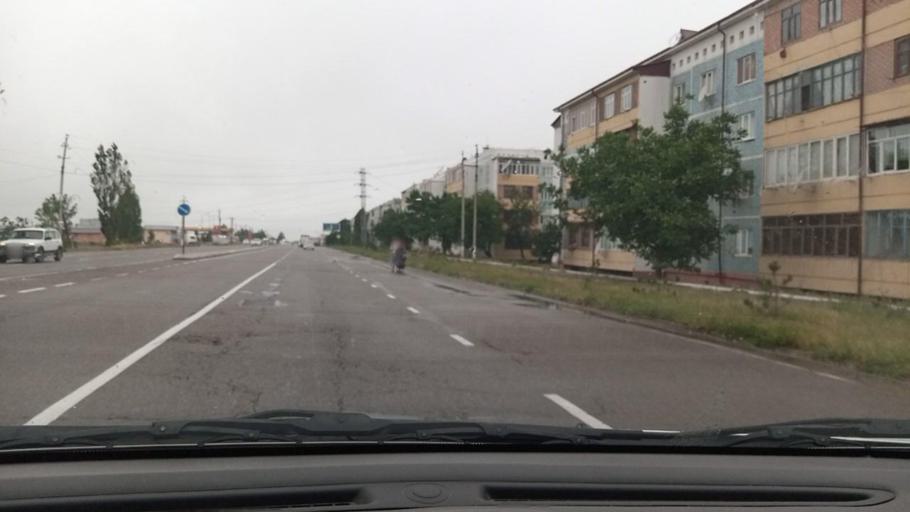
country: UZ
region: Toshkent
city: Angren
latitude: 41.0119
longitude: 70.1016
